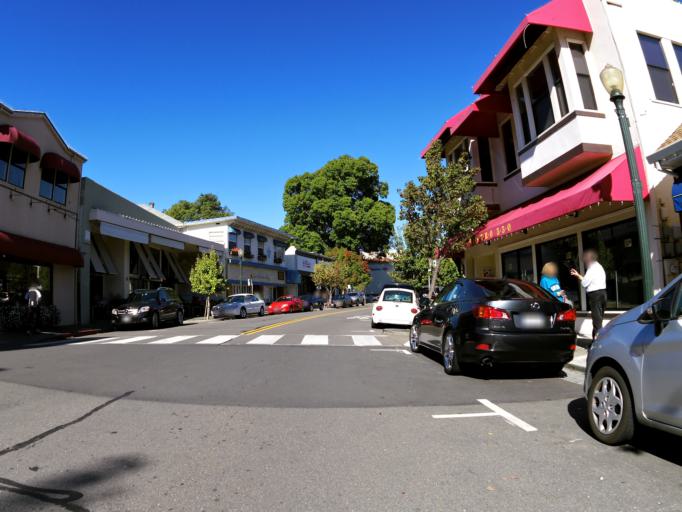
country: US
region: California
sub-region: Marin County
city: San Anselmo
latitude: 37.9729
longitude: -122.5621
